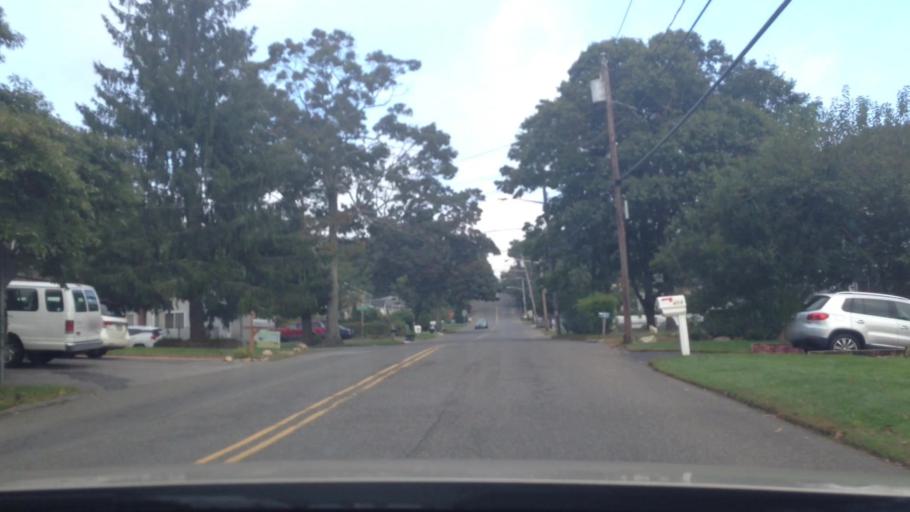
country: US
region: New York
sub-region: Suffolk County
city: Farmingville
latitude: 40.8363
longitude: -73.0346
